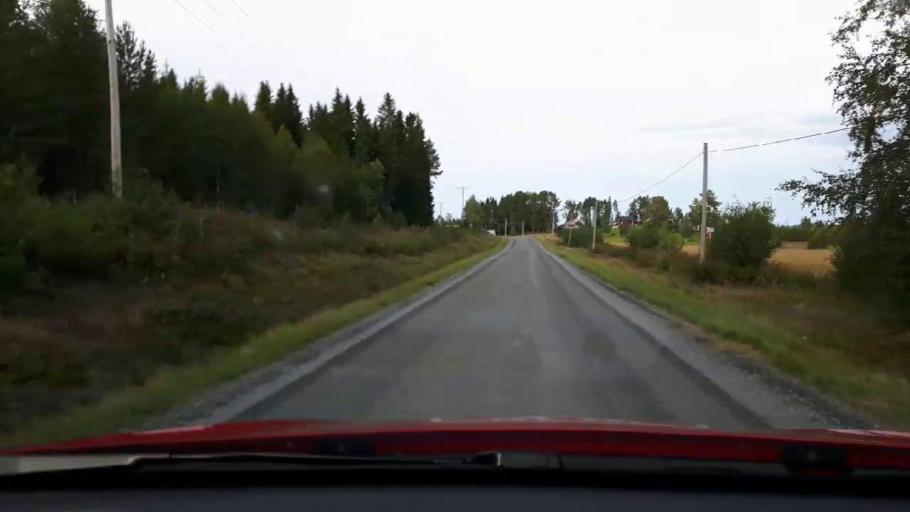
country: SE
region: Jaemtland
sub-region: Krokoms Kommun
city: Valla
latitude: 63.2539
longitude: 13.9490
